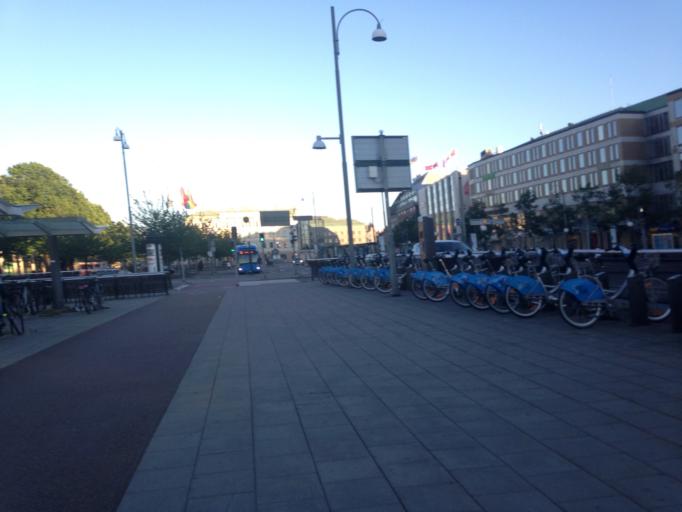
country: SE
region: Vaestra Goetaland
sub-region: Goteborg
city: Goeteborg
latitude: 57.7099
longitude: 11.9708
